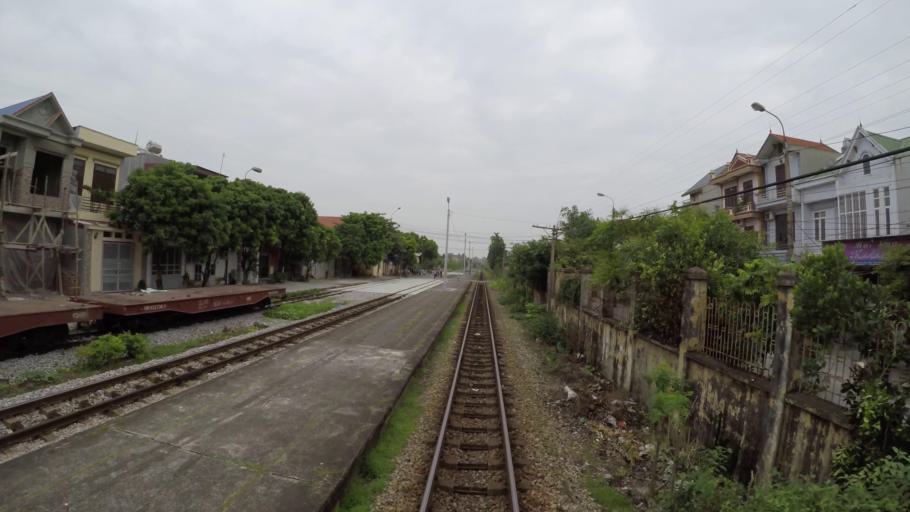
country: VN
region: Hai Duong
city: Phu Thai
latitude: 20.9732
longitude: 106.4844
